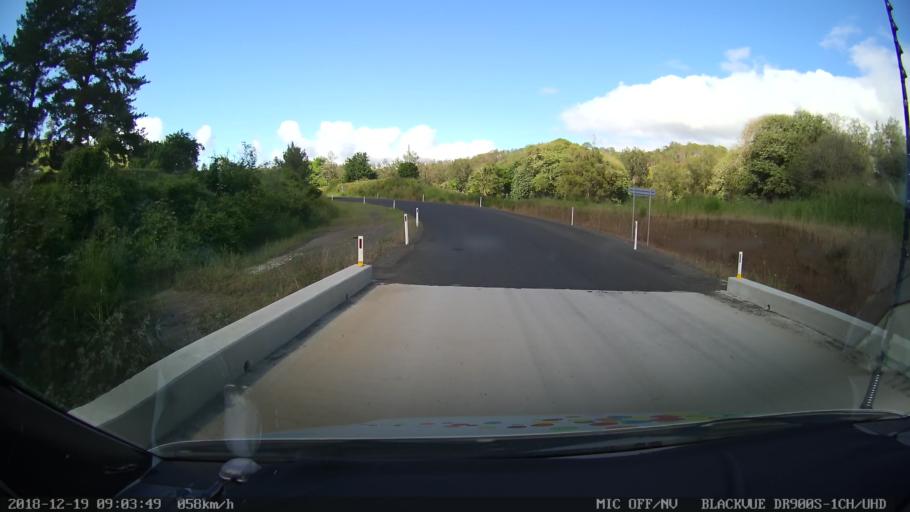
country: AU
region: New South Wales
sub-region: Kyogle
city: Kyogle
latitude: -28.4506
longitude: 152.9492
